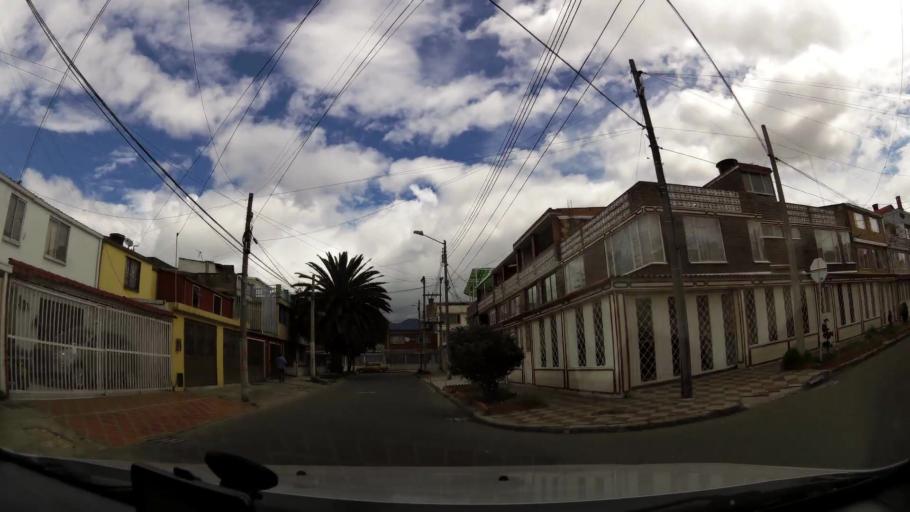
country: CO
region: Bogota D.C.
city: Bogota
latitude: 4.6000
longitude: -74.1221
